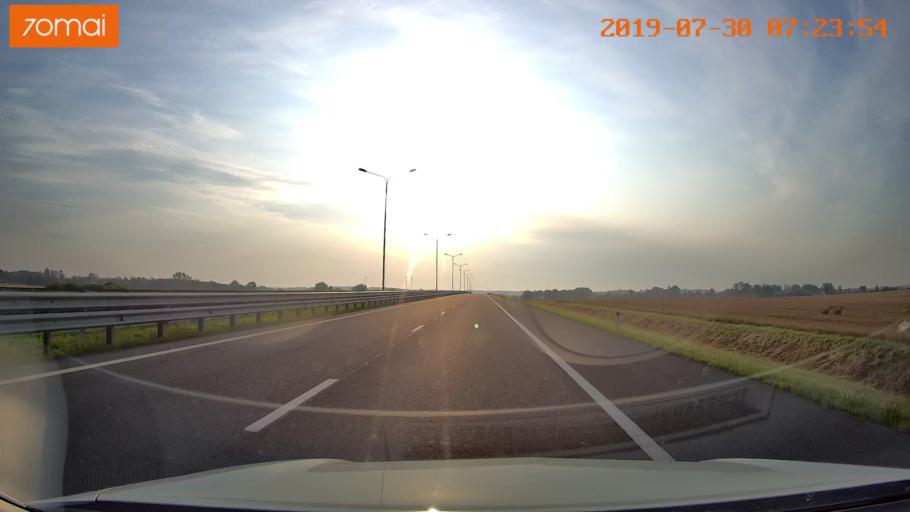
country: RU
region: Kaliningrad
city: Bol'shoe Isakovo
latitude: 54.6926
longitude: 20.7970
